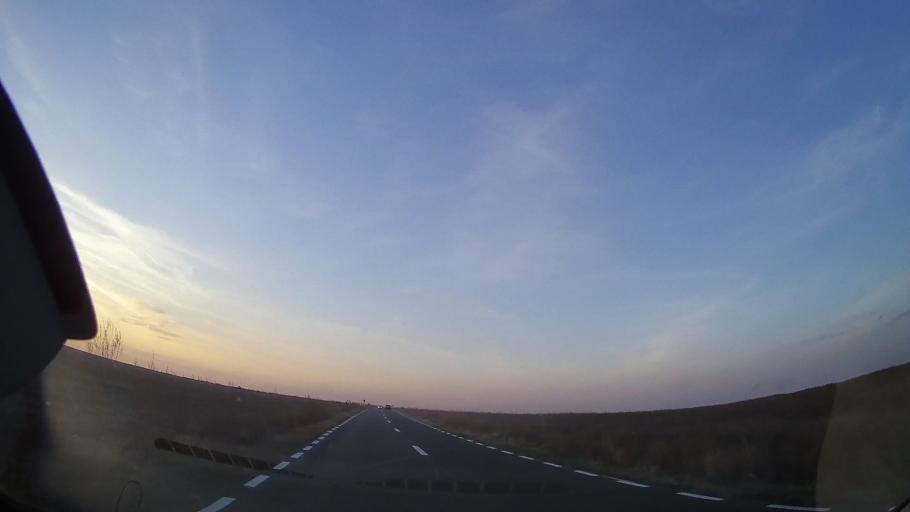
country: RO
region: Constanta
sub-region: Comuna Topraisar
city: Topraisar
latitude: 44.0166
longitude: 28.4293
